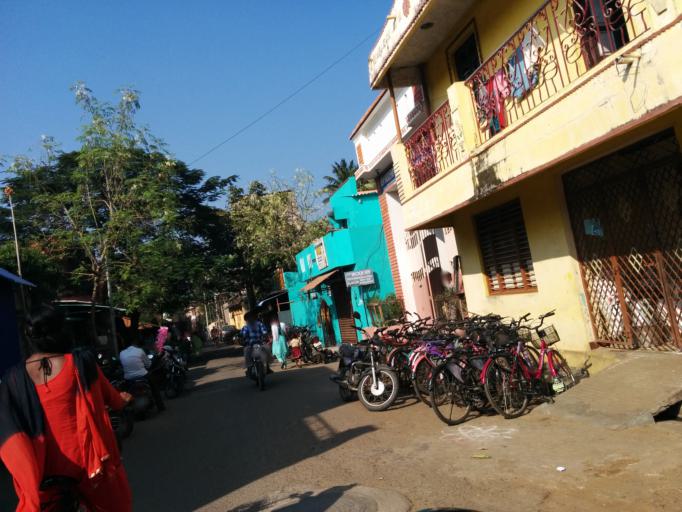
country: IN
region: Pondicherry
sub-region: Puducherry
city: Puducherry
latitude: 11.9477
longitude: 79.8347
